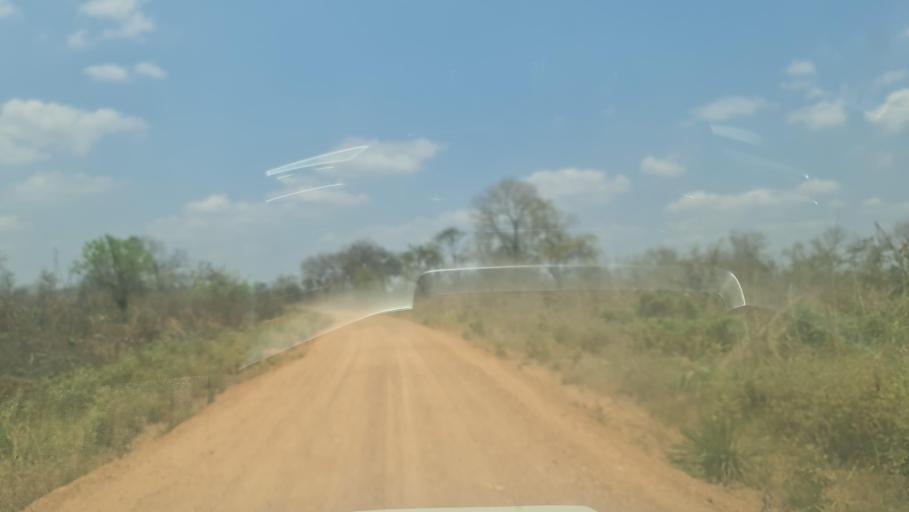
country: MW
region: Southern Region
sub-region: Nsanje District
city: Nsanje
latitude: -17.5675
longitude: 35.9027
